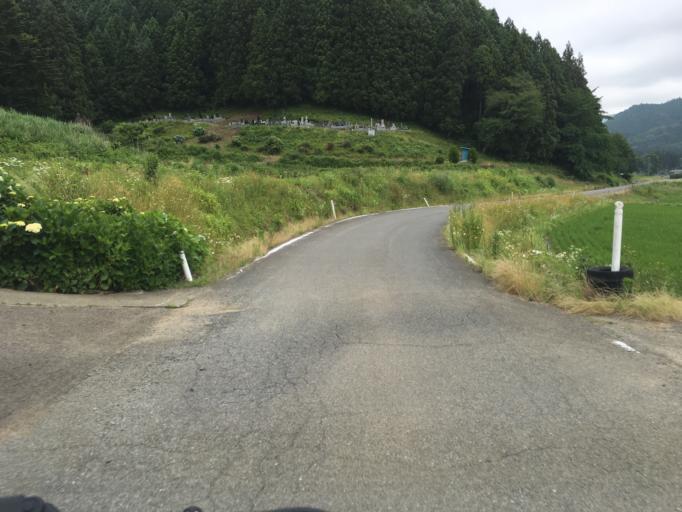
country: JP
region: Miyagi
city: Marumori
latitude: 37.7648
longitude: 140.8457
